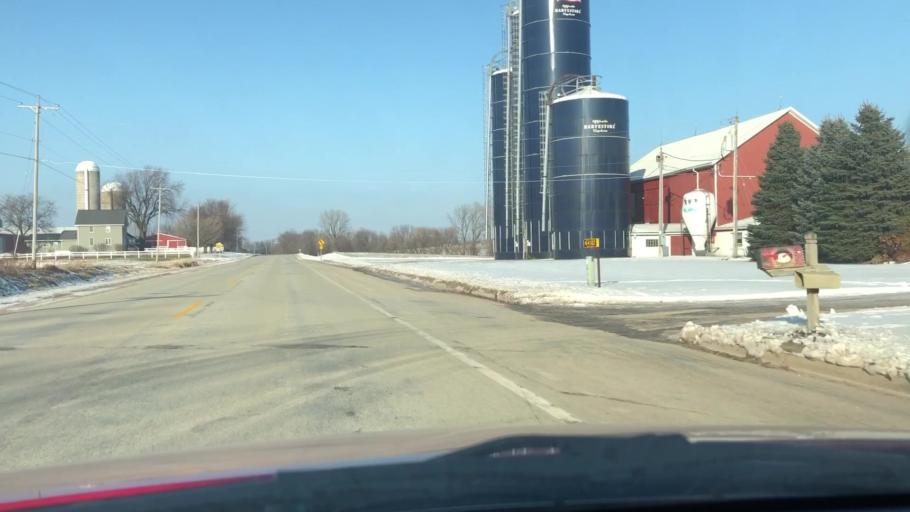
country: US
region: Wisconsin
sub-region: Outagamie County
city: Black Creek
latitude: 44.3899
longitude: -88.3746
